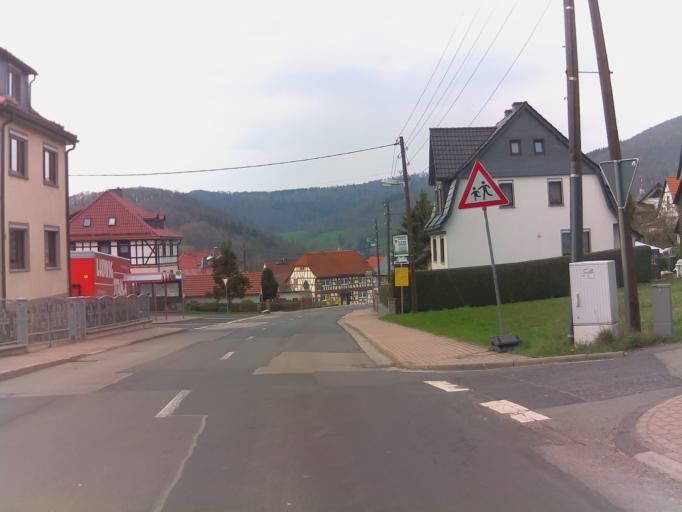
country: DE
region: Thuringia
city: Altersbach
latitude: 50.7435
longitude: 10.5084
